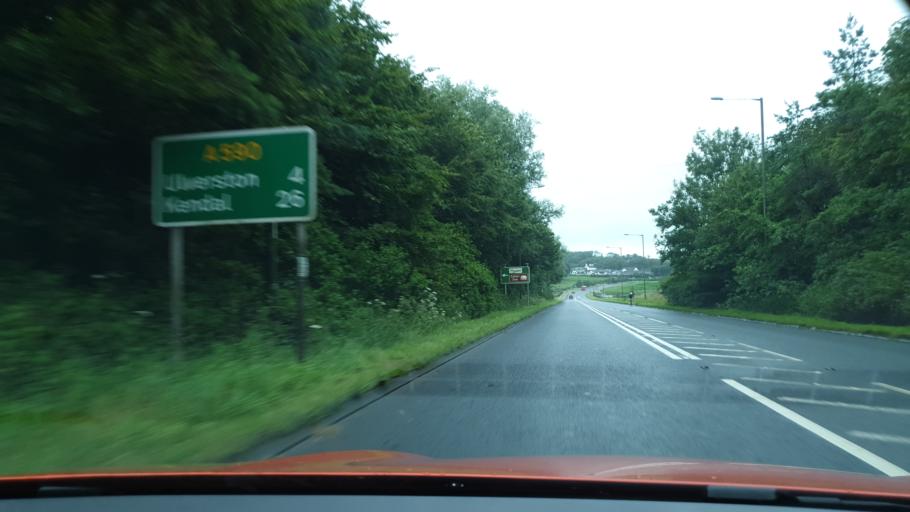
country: GB
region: England
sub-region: Cumbria
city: Dalton in Furness
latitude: 54.1674
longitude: -3.1605
